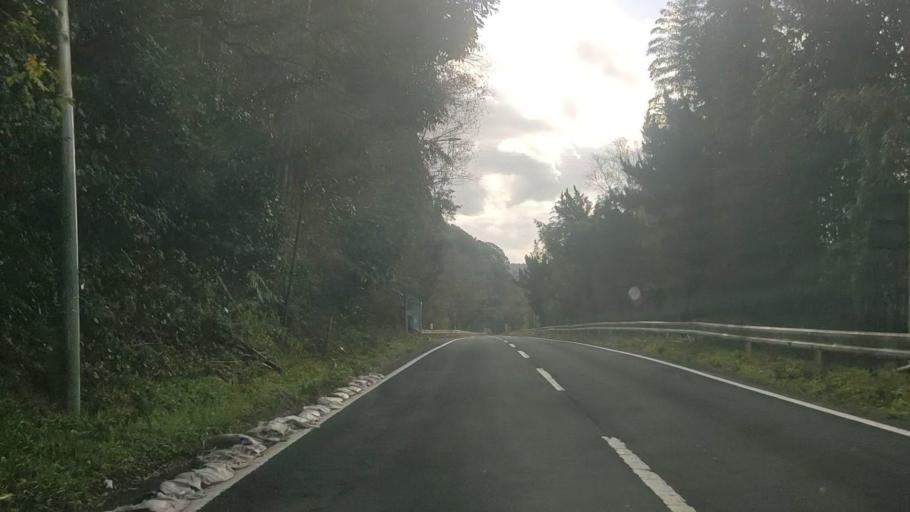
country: JP
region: Kagoshima
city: Okuchi-shinohara
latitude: 31.9707
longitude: 130.7404
